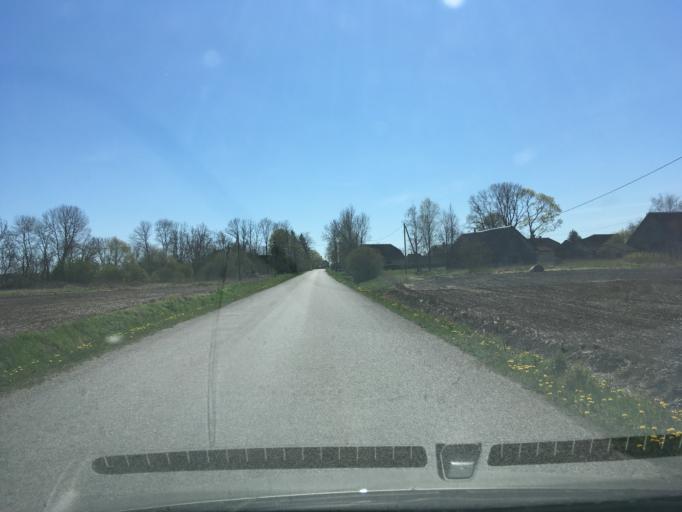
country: EE
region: Harju
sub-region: Raasiku vald
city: Arukula
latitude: 59.3928
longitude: 25.0796
